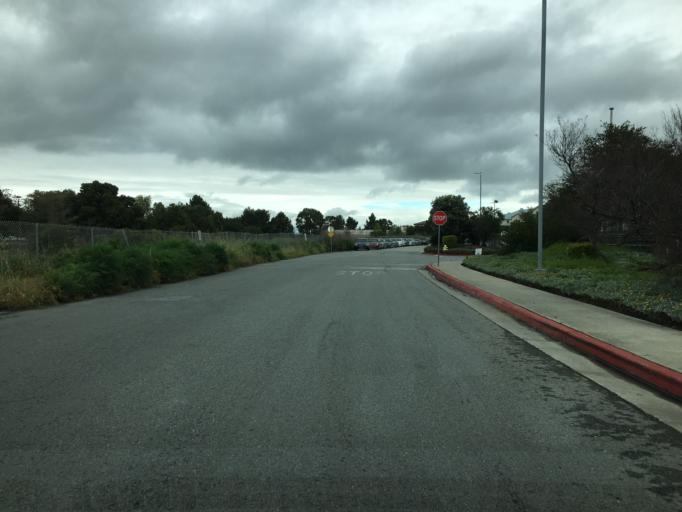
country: US
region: California
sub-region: San Mateo County
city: San Carlos
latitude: 37.5172
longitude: -122.2520
